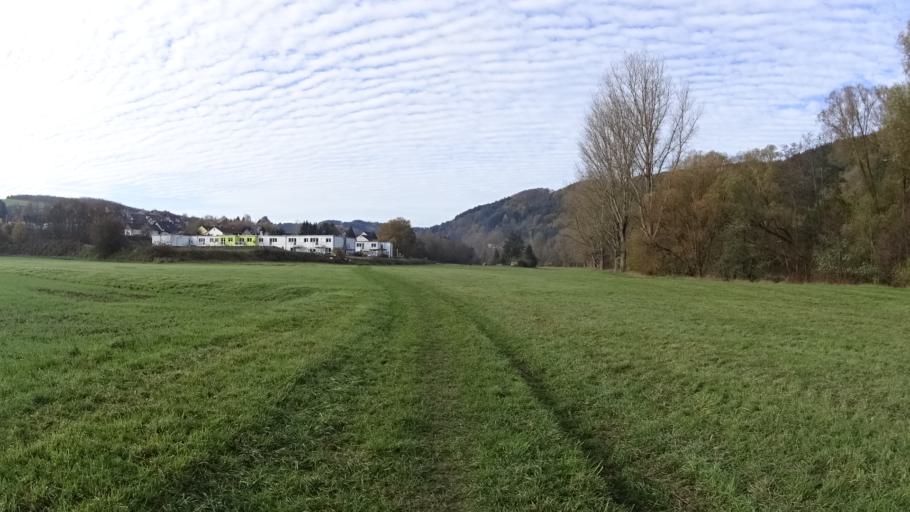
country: DE
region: Rheinland-Pfalz
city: Wiesweiler
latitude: 49.6279
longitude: 7.5639
